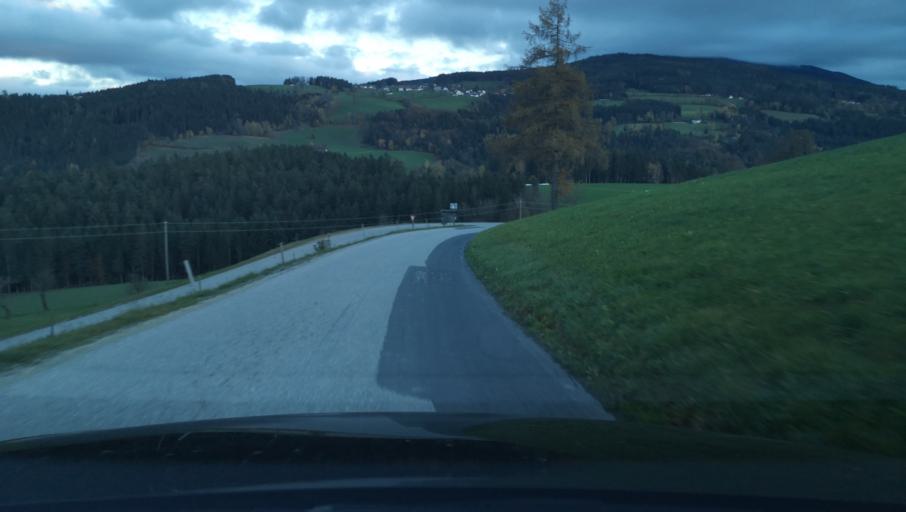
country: AT
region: Styria
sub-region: Politischer Bezirk Weiz
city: Koglhof
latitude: 47.3292
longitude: 15.6835
